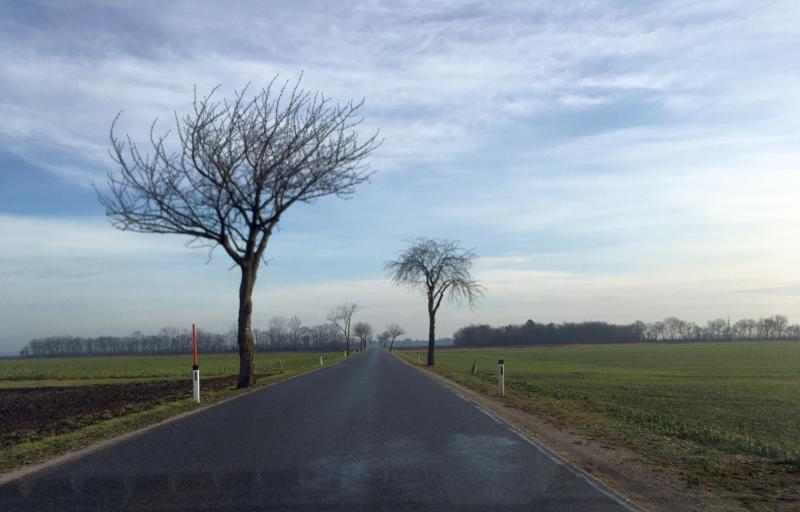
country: AT
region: Lower Austria
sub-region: Politischer Bezirk Ganserndorf
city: Andlersdorf
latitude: 48.1944
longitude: 16.6812
